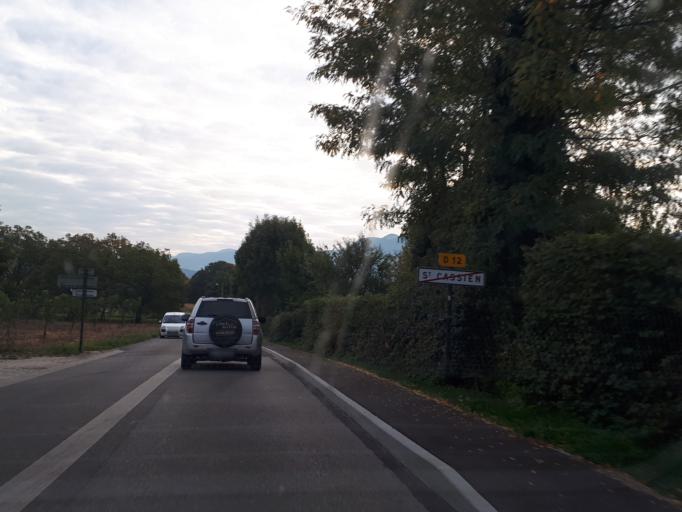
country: FR
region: Rhone-Alpes
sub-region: Departement de l'Isere
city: Saint-Cassien
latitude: 45.3582
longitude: 5.5615
